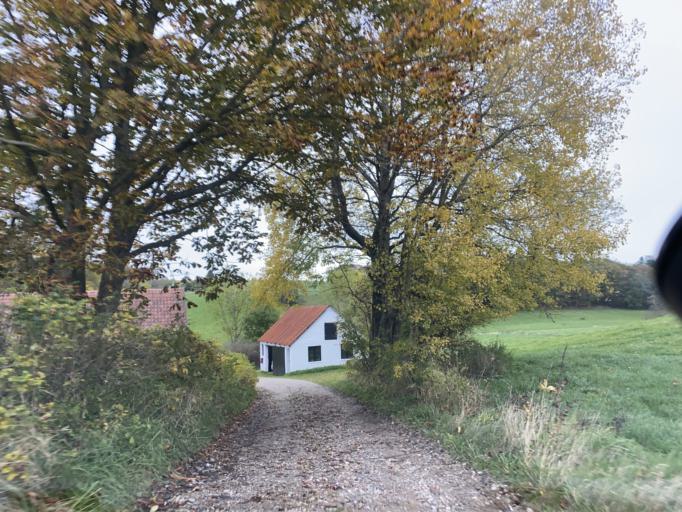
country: DK
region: Central Jutland
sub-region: Favrskov Kommune
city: Hammel
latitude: 56.1952
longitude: 9.7823
